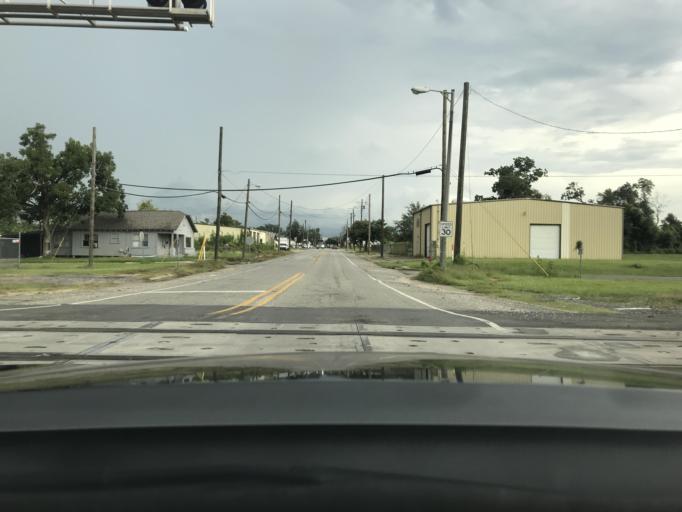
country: US
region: Louisiana
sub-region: Calcasieu Parish
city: Westlake
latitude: 30.2381
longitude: -93.2505
